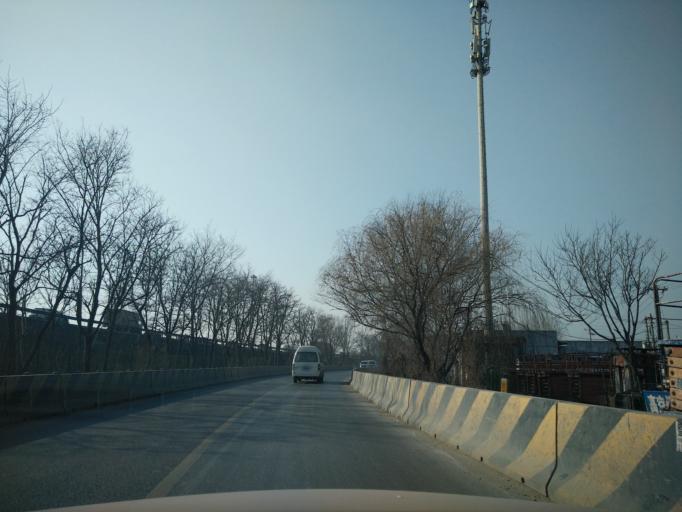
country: CN
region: Beijing
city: Jiugong
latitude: 39.8203
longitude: 116.5025
